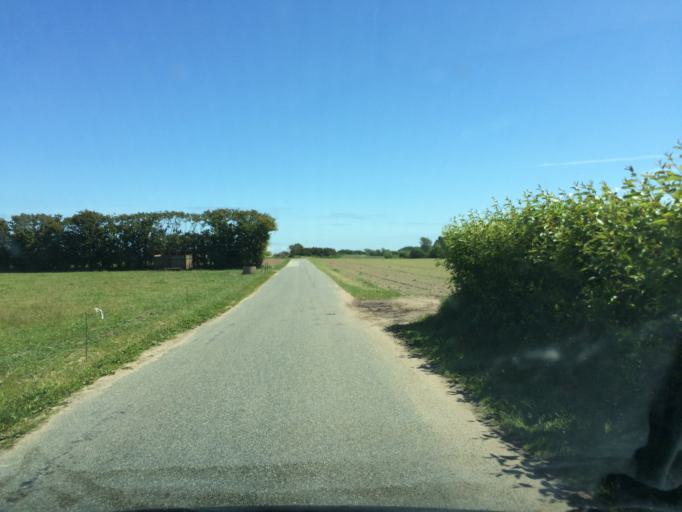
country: DK
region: Central Jutland
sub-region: Samso Kommune
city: Tranebjerg
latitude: 55.8325
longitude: 10.5443
